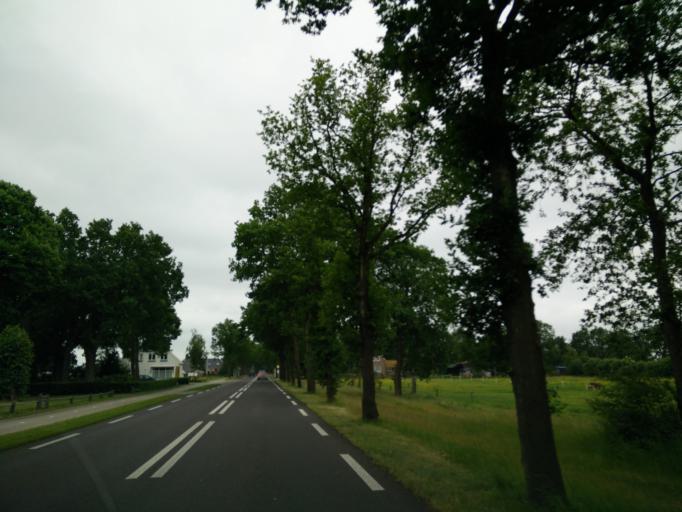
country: NL
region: Groningen
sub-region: Gemeente Groningen
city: Groningen
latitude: 53.1641
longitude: 6.4961
